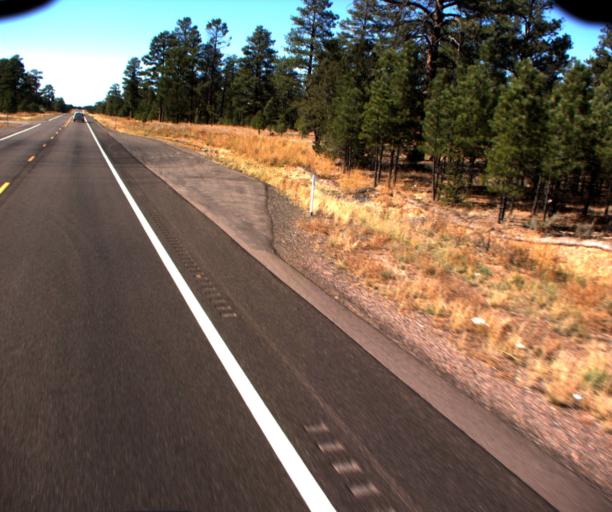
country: US
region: Arizona
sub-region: Apache County
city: Saint Michaels
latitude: 35.6995
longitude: -109.2870
